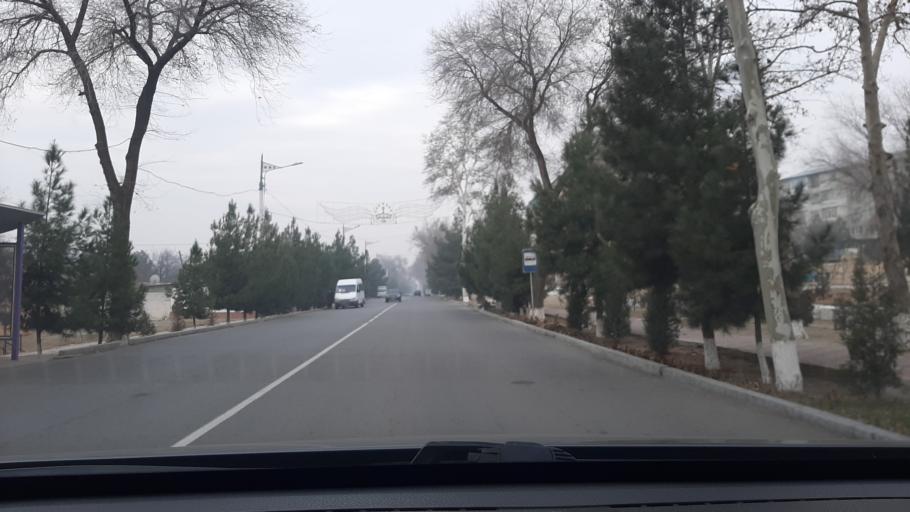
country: TJ
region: Viloyati Sughd
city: Palos
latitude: 40.2691
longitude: 69.8073
